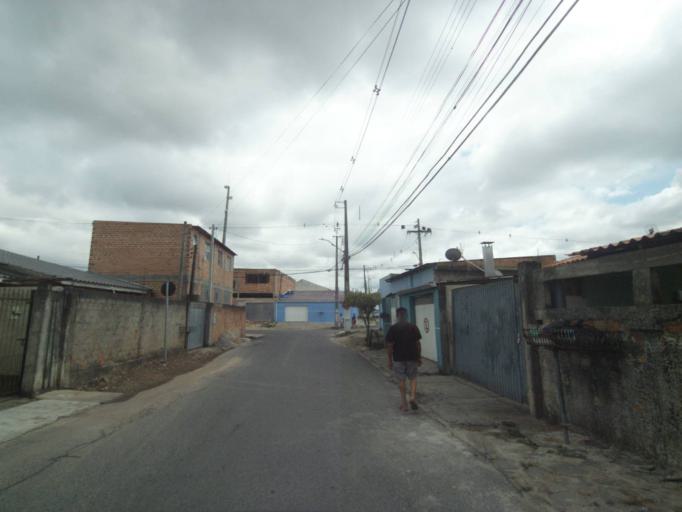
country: BR
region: Parana
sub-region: Pinhais
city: Pinhais
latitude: -25.4485
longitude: -49.1997
